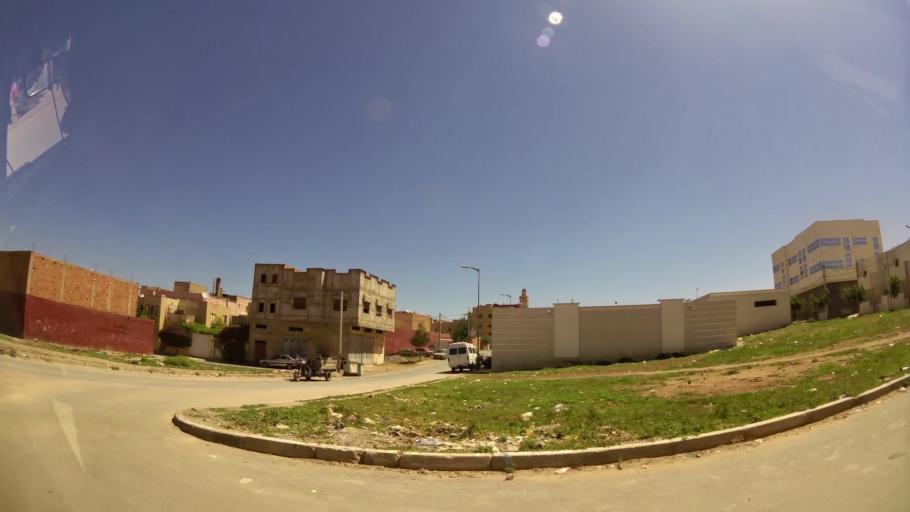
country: MA
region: Oriental
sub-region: Oujda-Angad
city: Oujda
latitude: 34.6593
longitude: -1.8793
